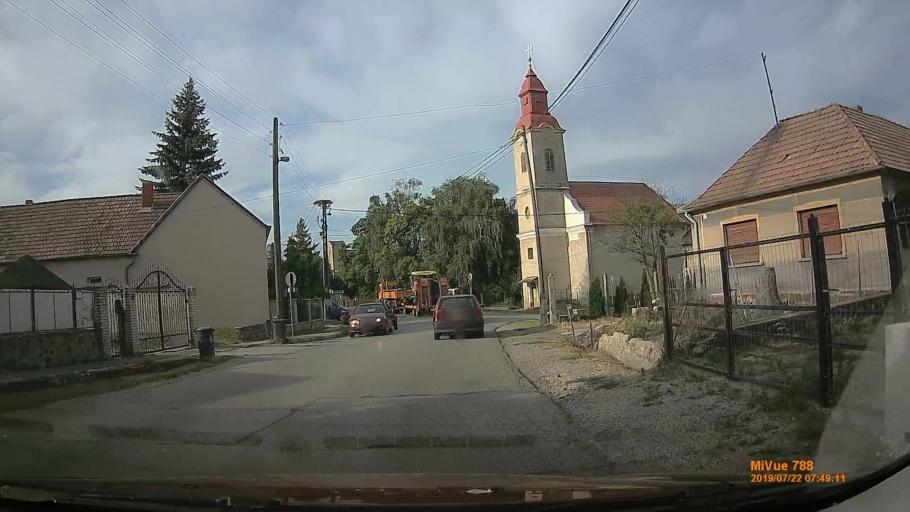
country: HU
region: Veszprem
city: Ajka
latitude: 47.0710
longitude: 17.5506
